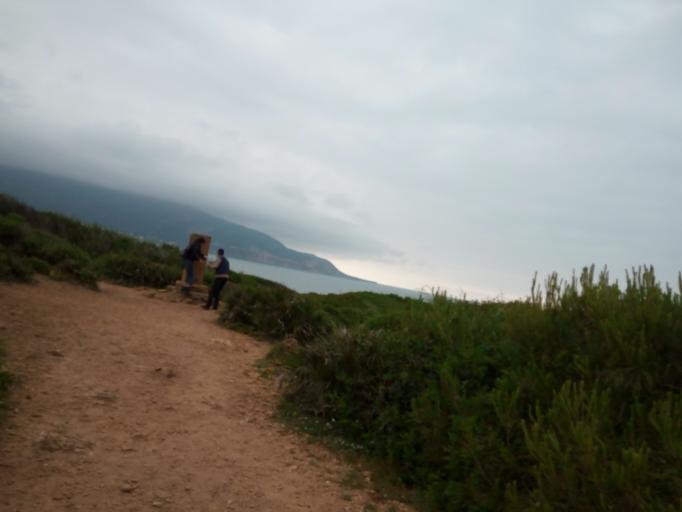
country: DZ
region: Tipaza
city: Tipasa
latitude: 36.5956
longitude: 2.4394
